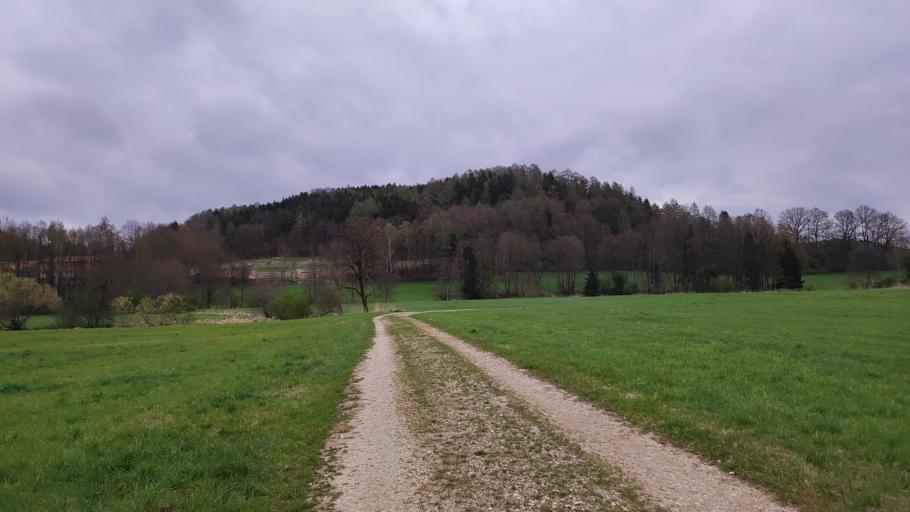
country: DE
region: Bavaria
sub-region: Swabia
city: Altenmunster
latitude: 48.4544
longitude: 10.5915
